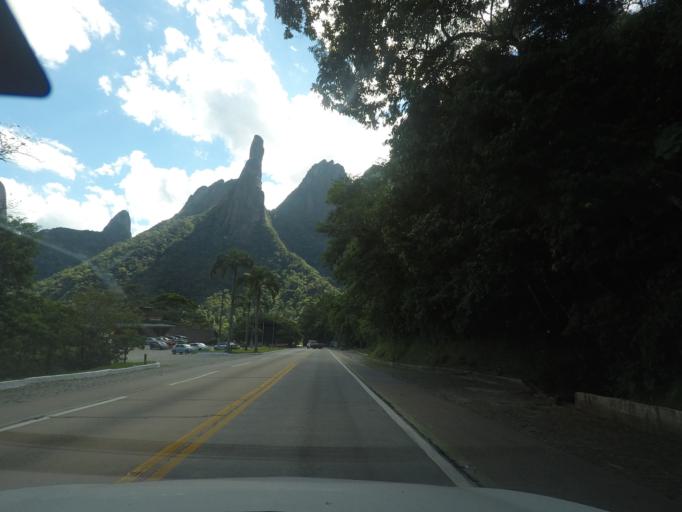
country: BR
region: Rio de Janeiro
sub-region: Teresopolis
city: Teresopolis
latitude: -22.4655
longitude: -42.9971
